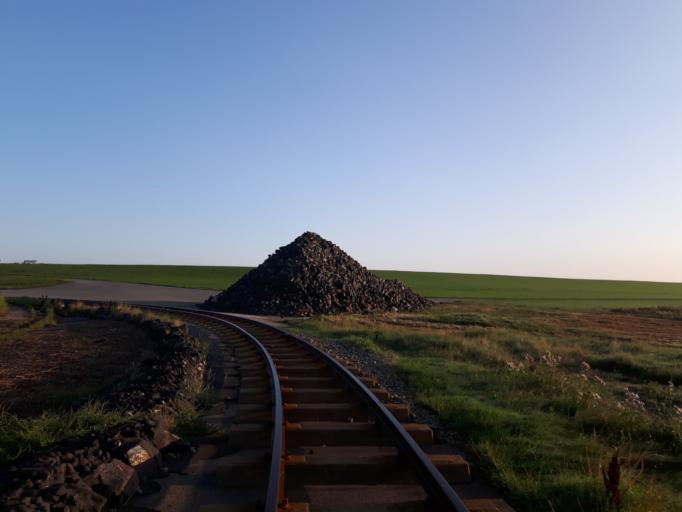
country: DE
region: Schleswig-Holstein
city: Dagebull
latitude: 54.7233
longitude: 8.7120
